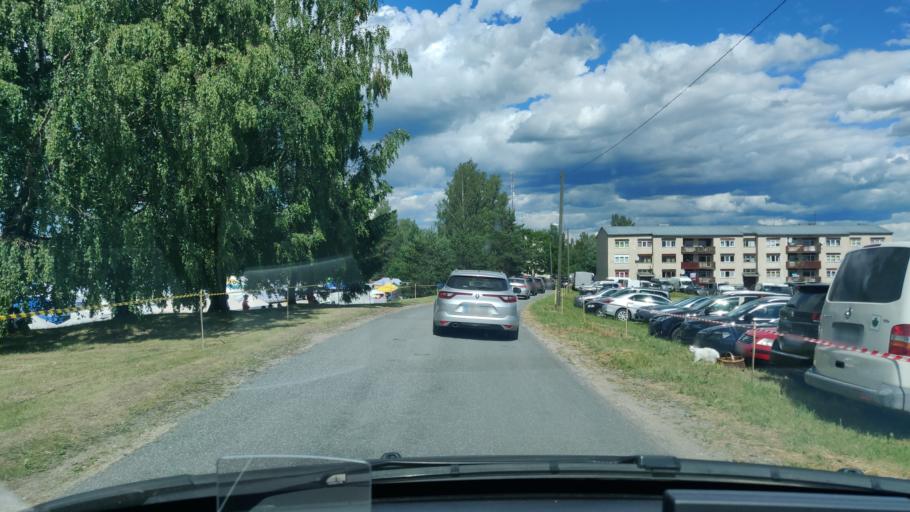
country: EE
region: Jogevamaa
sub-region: Mustvee linn
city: Mustvee
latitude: 58.9846
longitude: 26.8713
